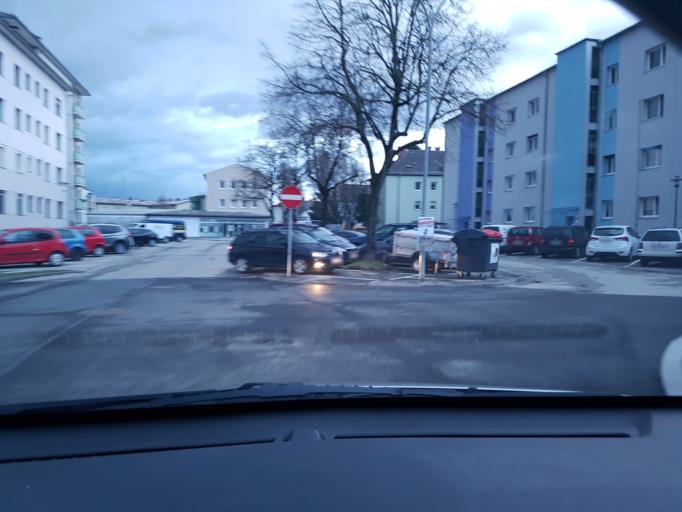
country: AT
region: Upper Austria
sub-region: Steyr Stadt
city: Steyr
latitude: 48.0476
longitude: 14.4229
